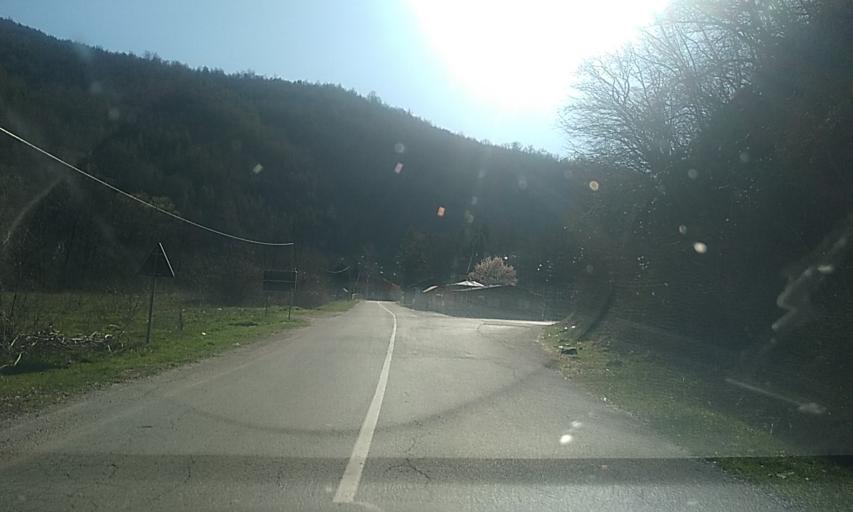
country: RS
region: Central Serbia
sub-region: Pcinjski Okrug
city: Bosilegrad
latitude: 42.4183
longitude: 22.5236
